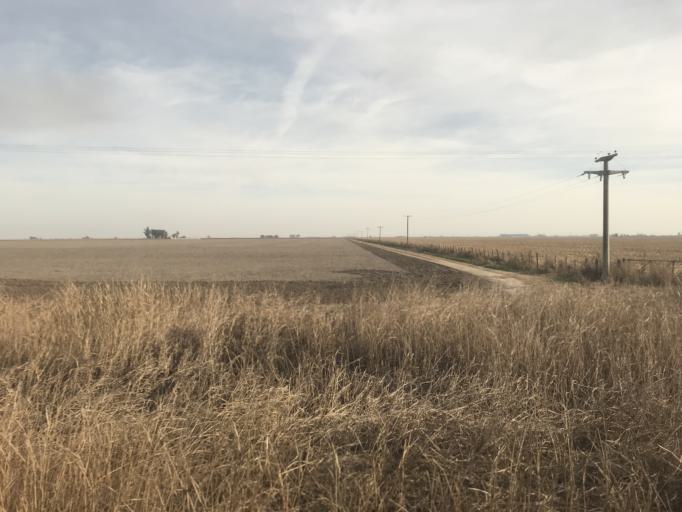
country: AR
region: Cordoba
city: Pilar
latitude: -31.7284
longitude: -63.8454
